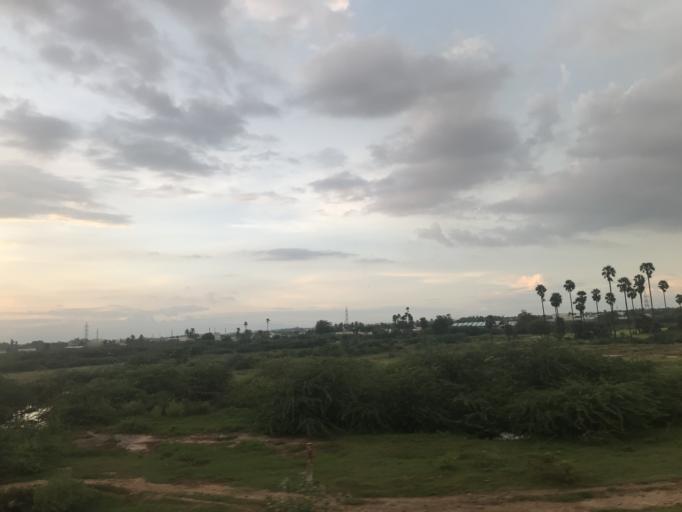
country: IN
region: Tamil Nadu
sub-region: Tiruppur
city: Tiruppur
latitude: 11.1323
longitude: 77.3720
